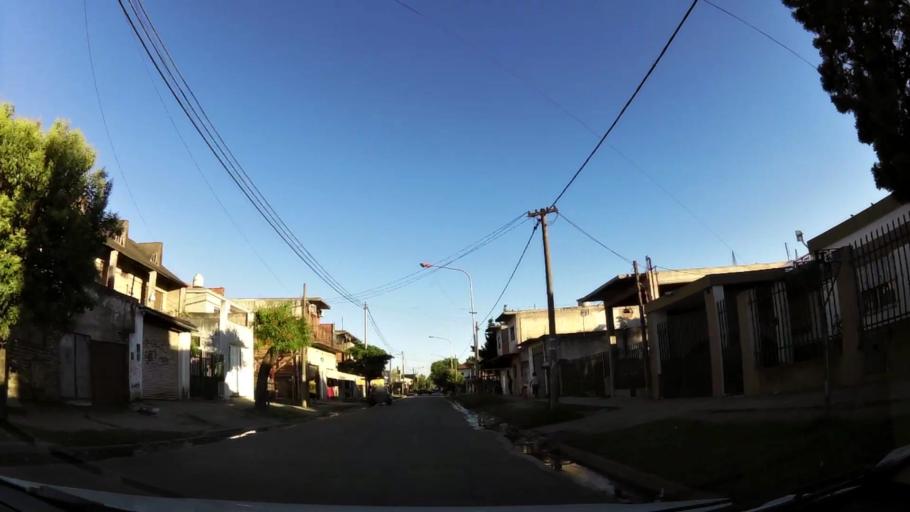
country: AR
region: Buenos Aires
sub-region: Partido de Moron
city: Moron
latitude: -34.7178
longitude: -58.6125
